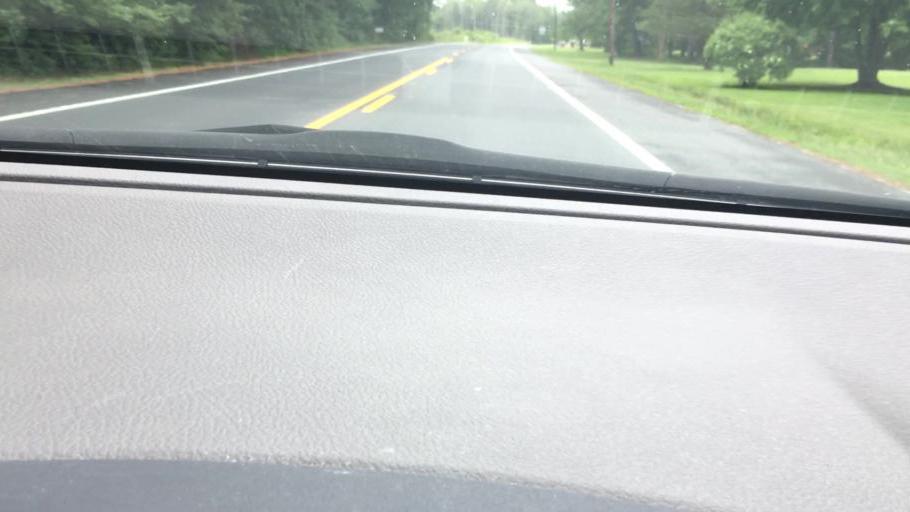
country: US
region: Maryland
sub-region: Worcester County
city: Pocomoke City
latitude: 38.0655
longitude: -75.5226
